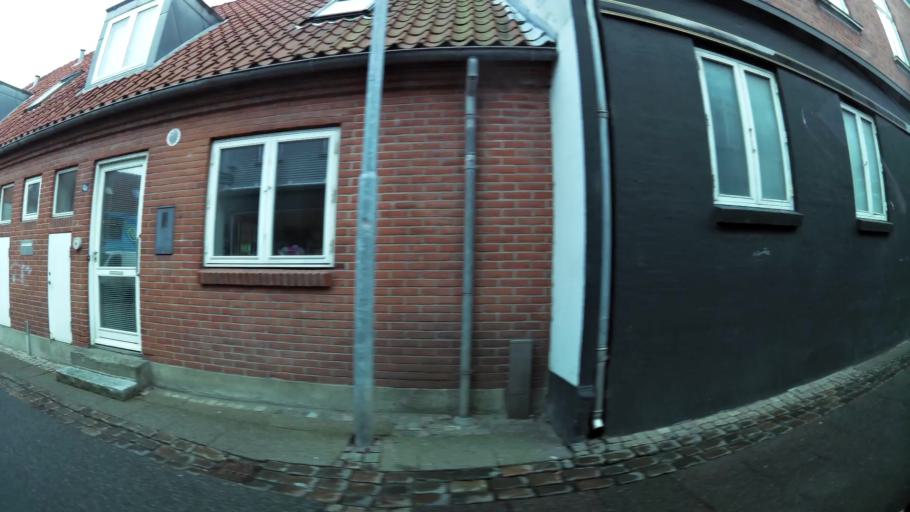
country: DK
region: North Denmark
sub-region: Thisted Kommune
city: Thisted
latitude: 56.9561
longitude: 8.6925
